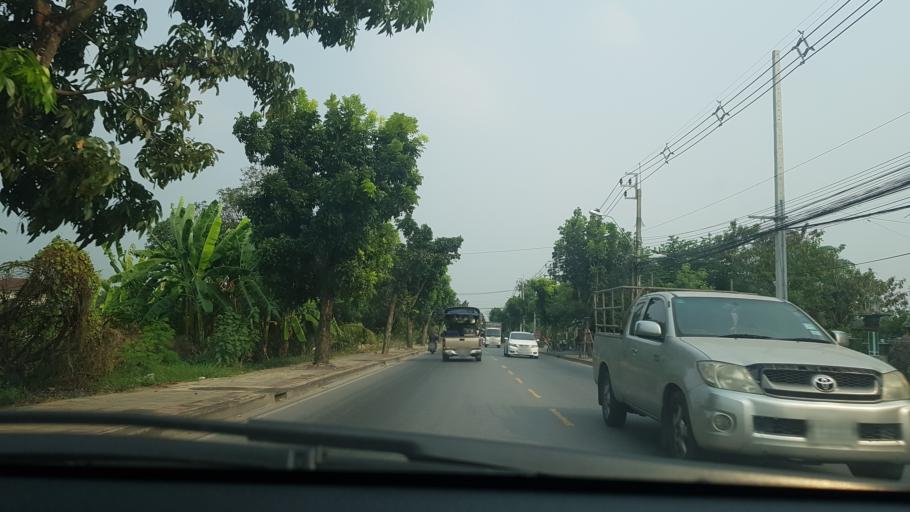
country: TH
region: Bangkok
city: Thawi Watthana
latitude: 13.7568
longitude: 100.3874
